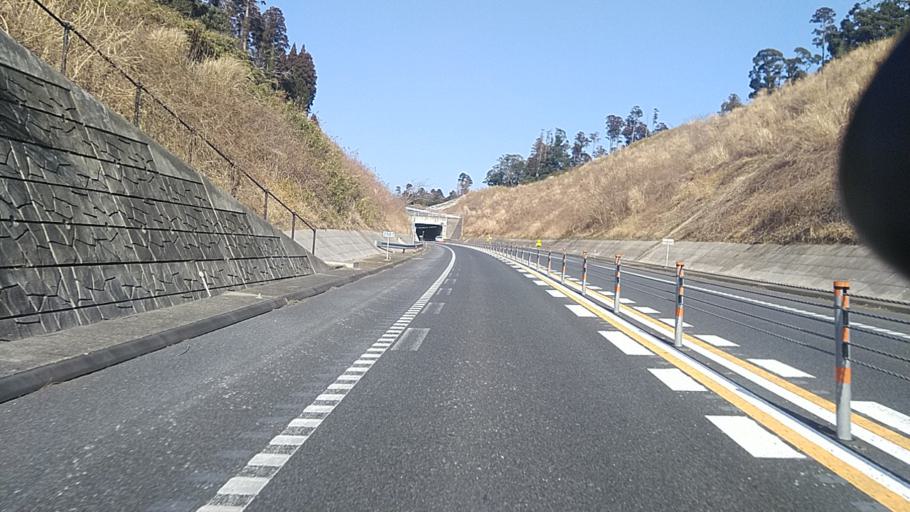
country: JP
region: Chiba
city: Oami
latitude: 35.5538
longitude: 140.3150
